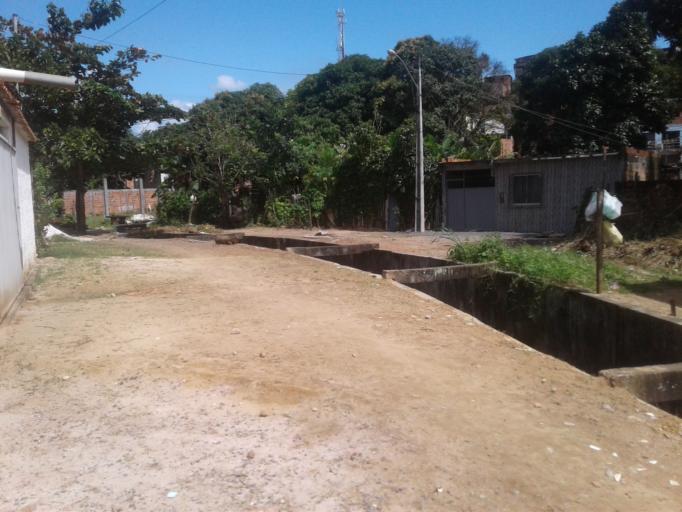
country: BR
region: Bahia
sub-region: Salvador
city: Salvador
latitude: -12.8812
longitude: -38.4735
